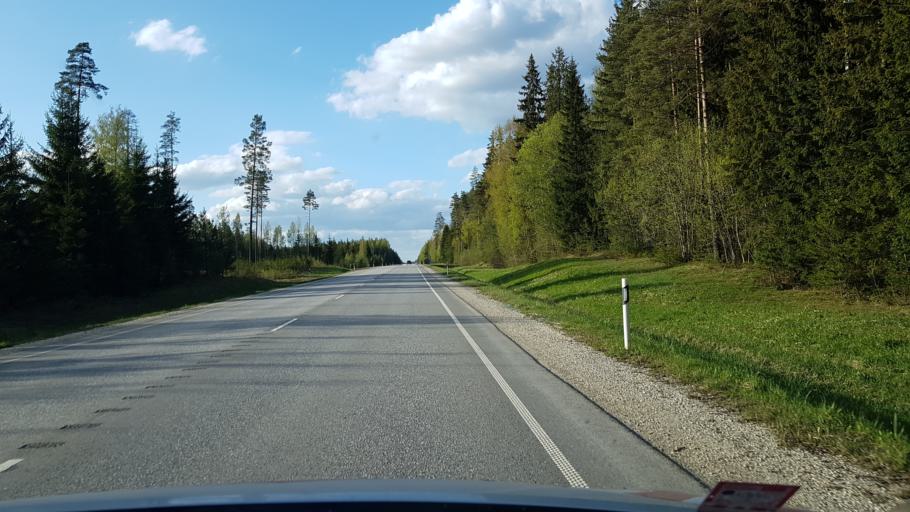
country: EE
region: Vorumaa
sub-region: Voru linn
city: Voru
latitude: 57.9462
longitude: 26.7954
